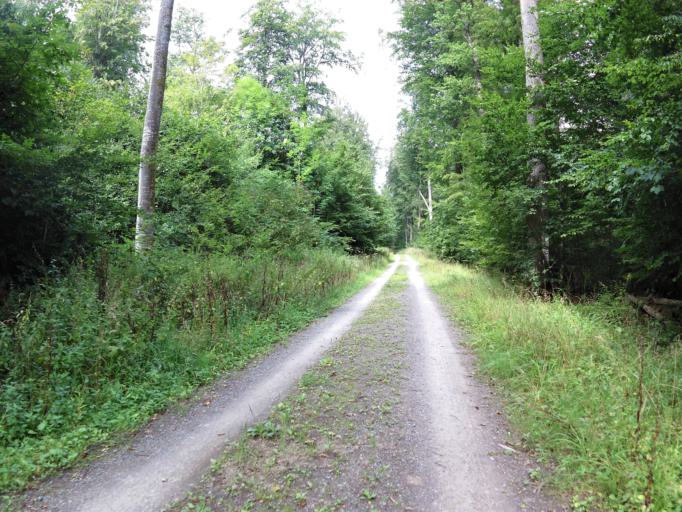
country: DE
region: Bavaria
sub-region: Regierungsbezirk Unterfranken
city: Kleinrinderfeld
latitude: 49.7163
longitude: 9.8282
